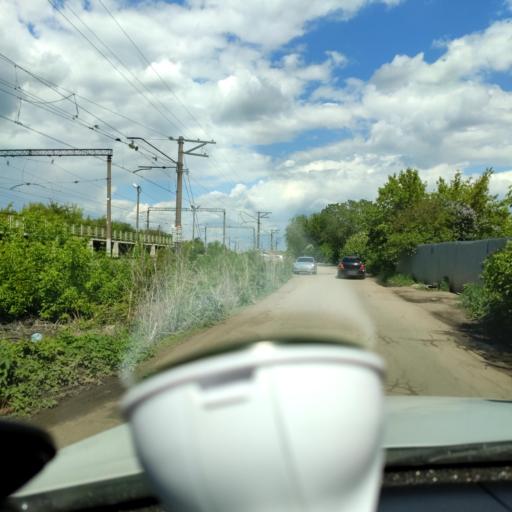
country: RU
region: Samara
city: Petra-Dubrava
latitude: 53.2708
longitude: 50.3180
